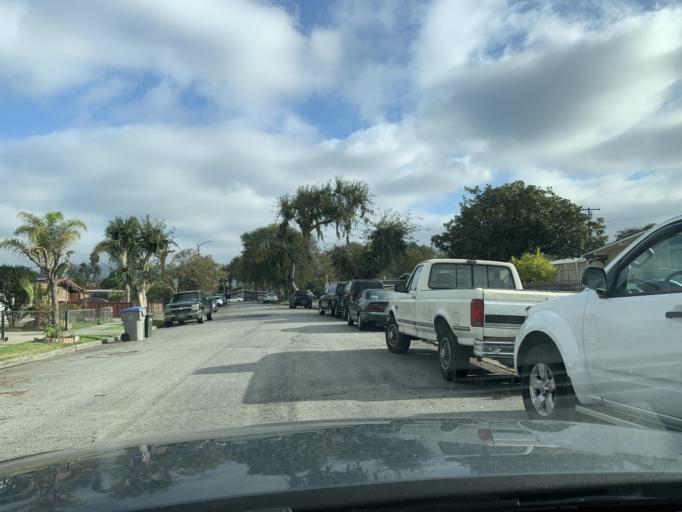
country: US
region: California
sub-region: Santa Clara County
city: Alum Rock
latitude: 37.3362
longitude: -121.8428
